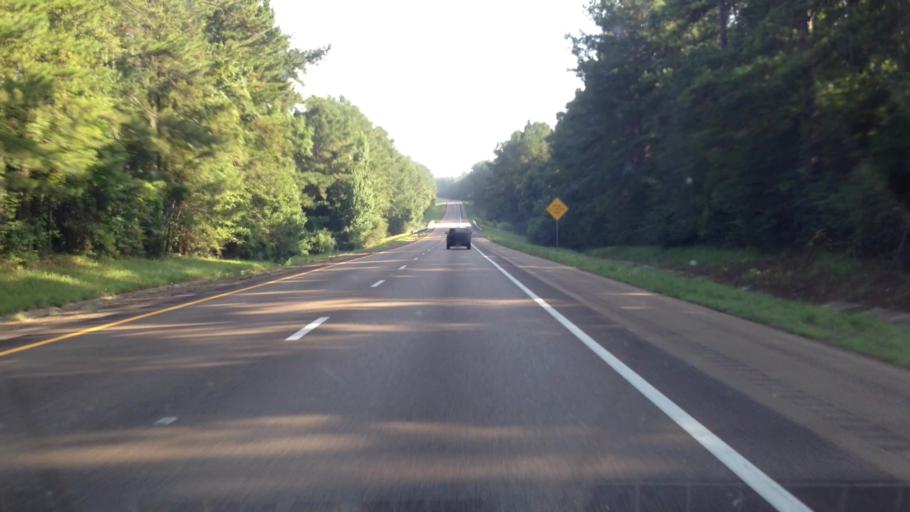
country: US
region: Mississippi
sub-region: Pike County
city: Summit
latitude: 31.3232
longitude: -90.4772
